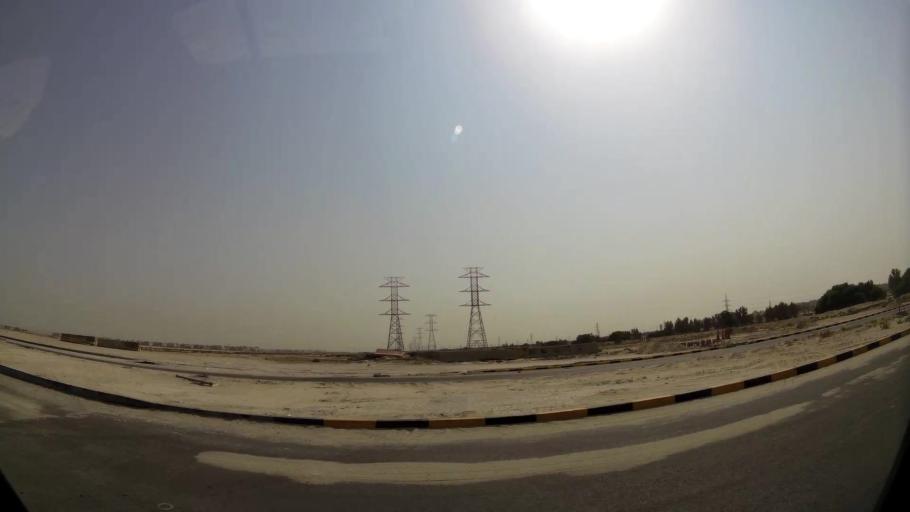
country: KW
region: Muhafazat al Jahra'
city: Al Jahra'
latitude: 29.3355
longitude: 47.7405
